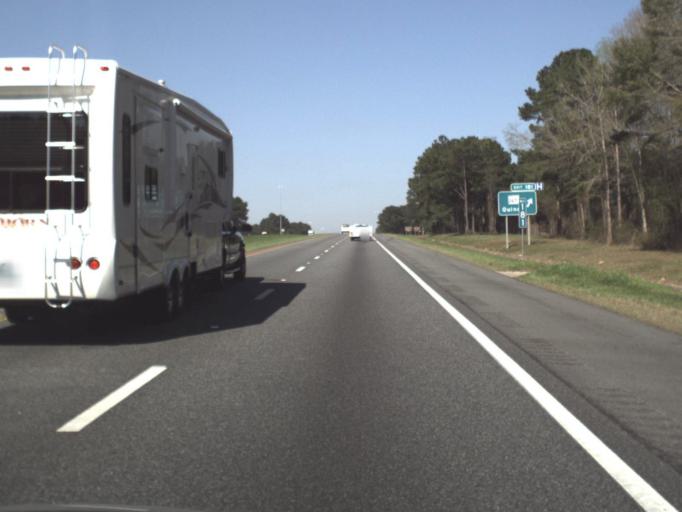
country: US
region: Florida
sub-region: Gadsden County
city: Quincy
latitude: 30.5361
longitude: -84.5870
